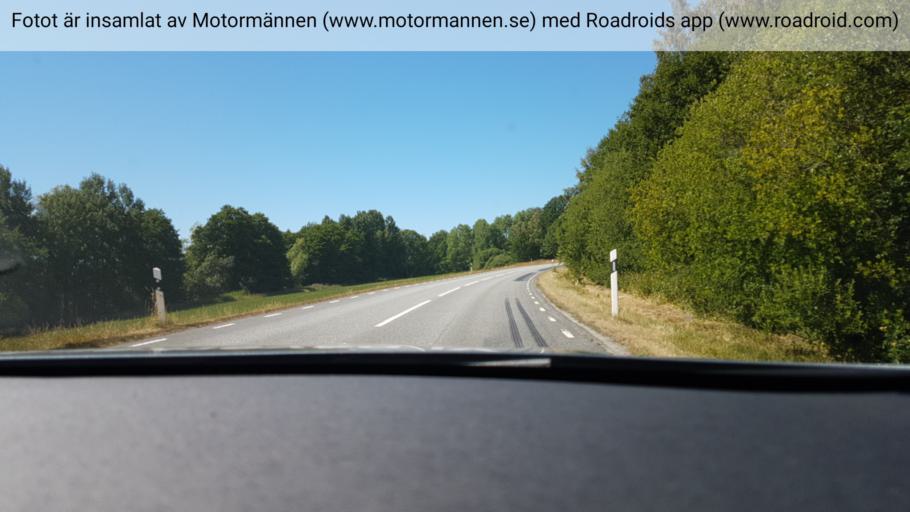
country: SE
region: Joenkoeping
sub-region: Jonkopings Kommun
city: Asa
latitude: 58.0013
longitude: 14.7213
